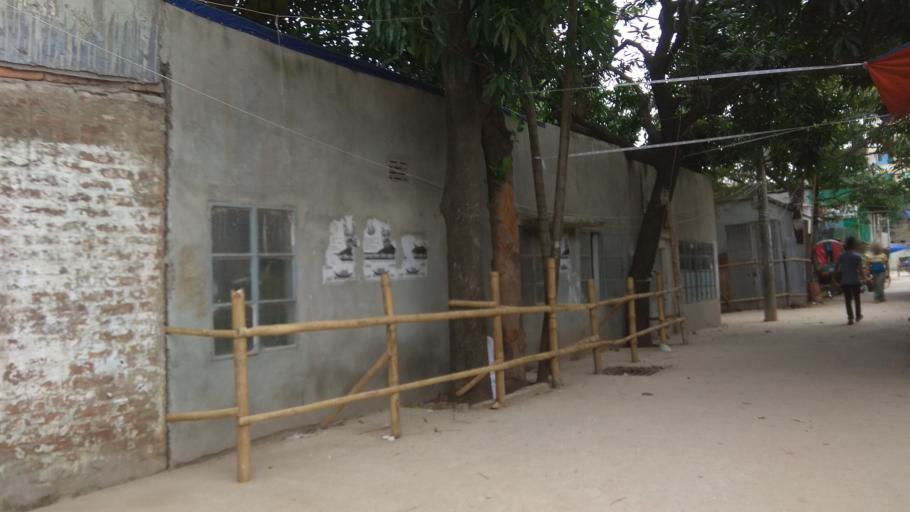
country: BD
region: Dhaka
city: Tungi
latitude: 23.8211
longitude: 90.3558
